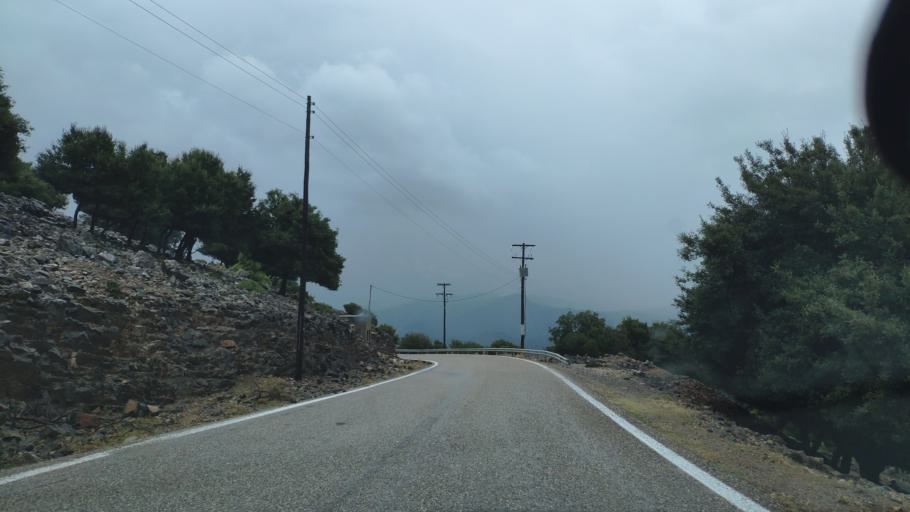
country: GR
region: Central Greece
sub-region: Nomos Evrytanias
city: Kerasochori
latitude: 39.0806
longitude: 21.4057
